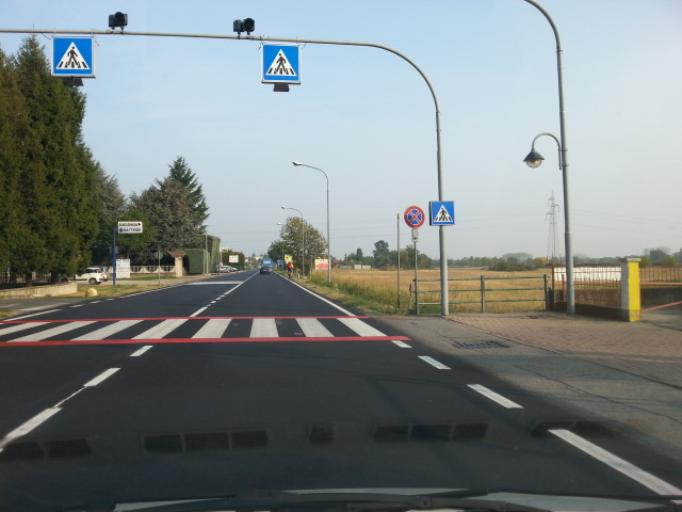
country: IT
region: Piedmont
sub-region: Provincia di Torino
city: Sangano
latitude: 45.0255
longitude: 7.4545
